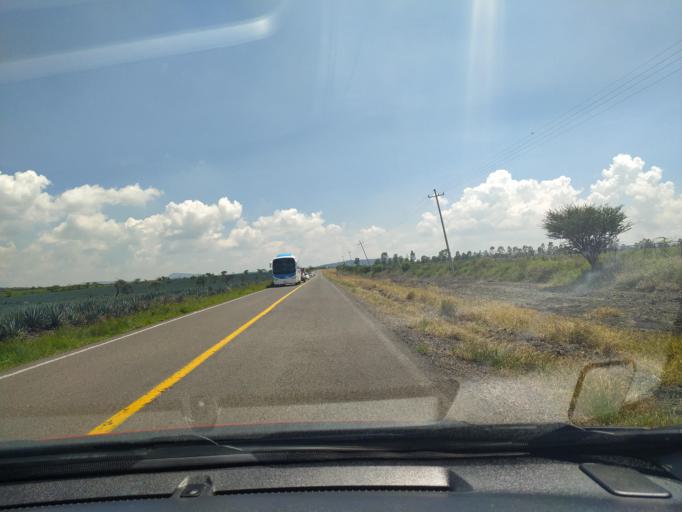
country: MX
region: Guanajuato
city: Ciudad Manuel Doblado
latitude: 20.6817
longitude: -101.9368
